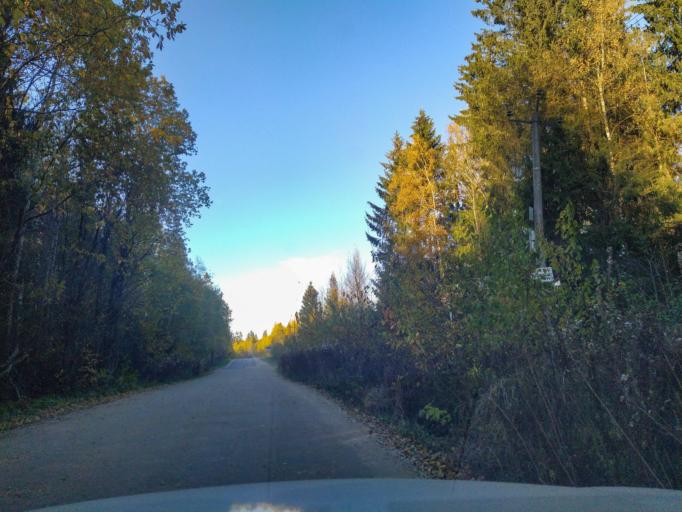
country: RU
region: Leningrad
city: Siverskiy
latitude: 59.2986
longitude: 30.0348
